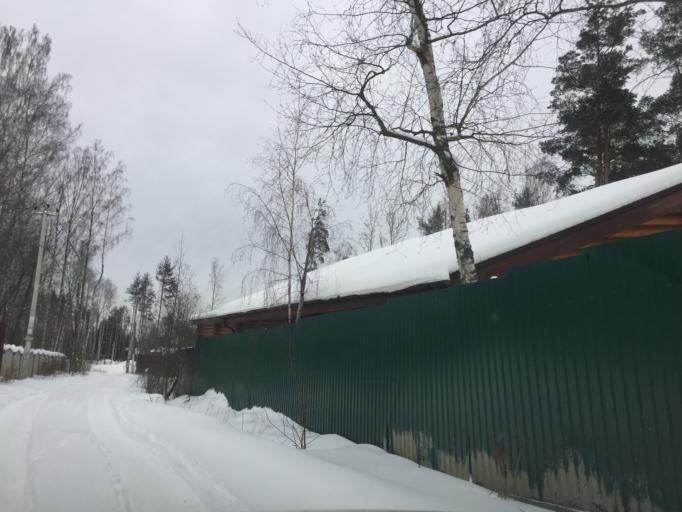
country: RU
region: Leningrad
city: Otradnoye
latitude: 59.7809
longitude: 30.7837
